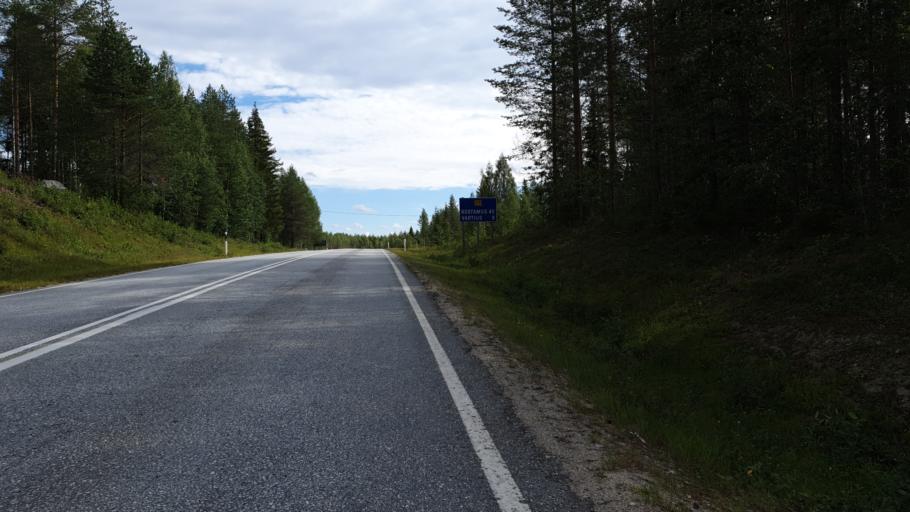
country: FI
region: Kainuu
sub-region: Kehys-Kainuu
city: Kuhmo
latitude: 64.4951
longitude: 29.9051
